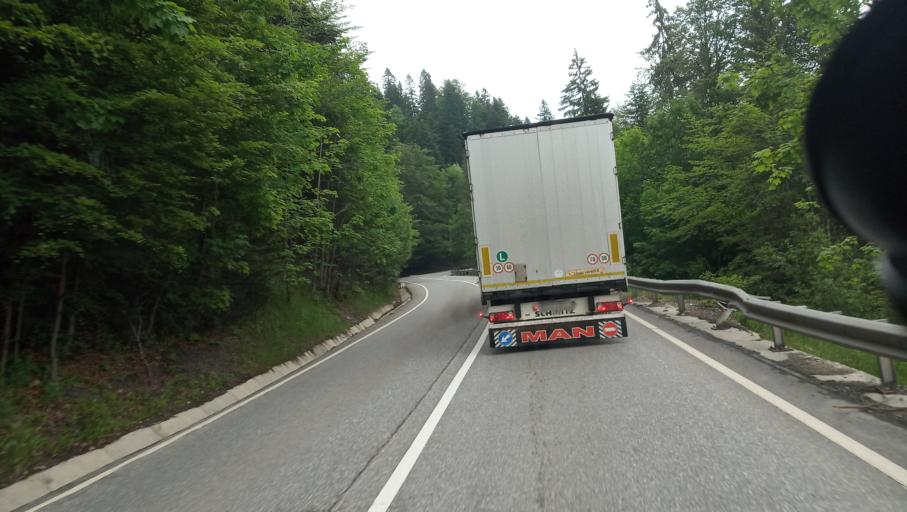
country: RO
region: Neamt
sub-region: Comuna Pipirig
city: Dolhesti
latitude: 47.1678
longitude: 26.0088
